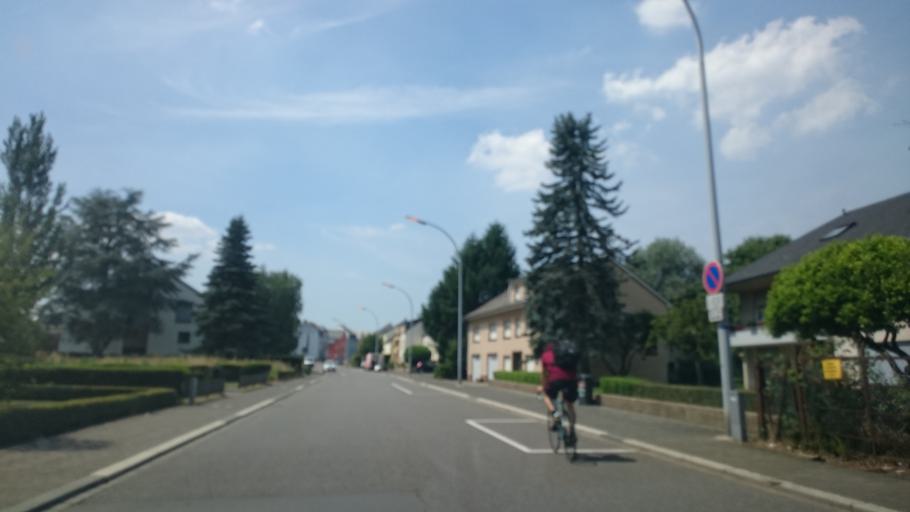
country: LU
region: Luxembourg
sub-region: Canton de Capellen
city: Mamer
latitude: 49.6272
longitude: 6.0302
